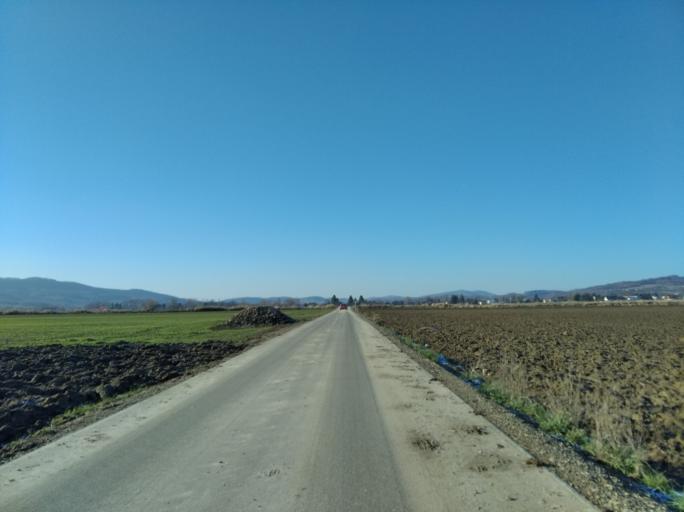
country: PL
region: Subcarpathian Voivodeship
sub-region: Powiat strzyzowski
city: Wisniowa
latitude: 49.8671
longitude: 21.6975
